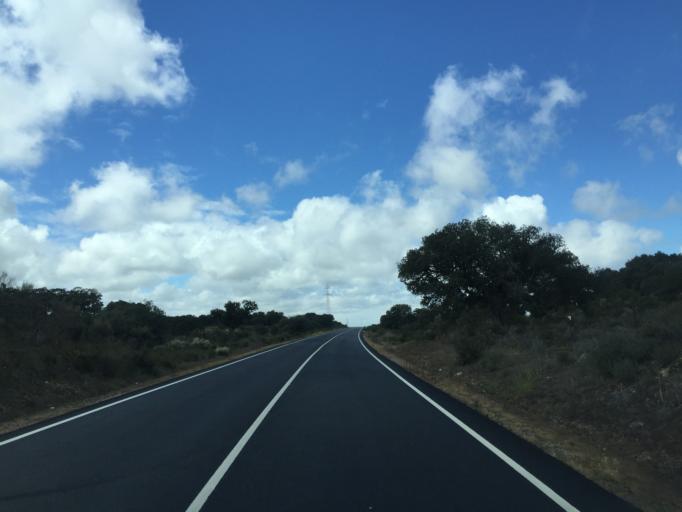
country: ES
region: Castille and Leon
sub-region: Provincia de Zamora
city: Moral de Sayago
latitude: 41.4830
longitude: -6.1157
